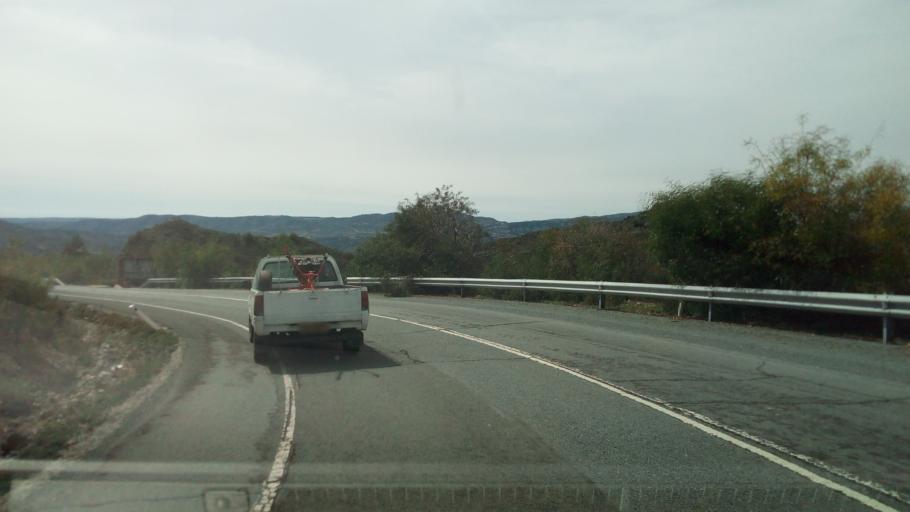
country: CY
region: Limassol
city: Pelendri
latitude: 34.8756
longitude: 32.9354
